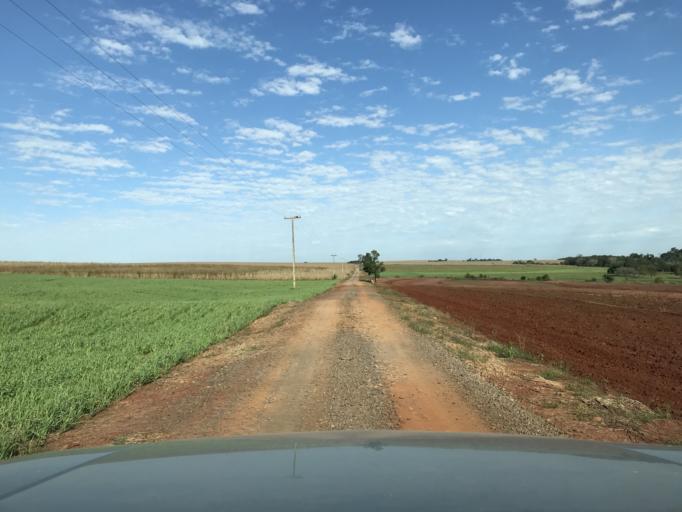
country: BR
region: Parana
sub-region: Palotina
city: Palotina
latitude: -24.1629
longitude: -53.7486
